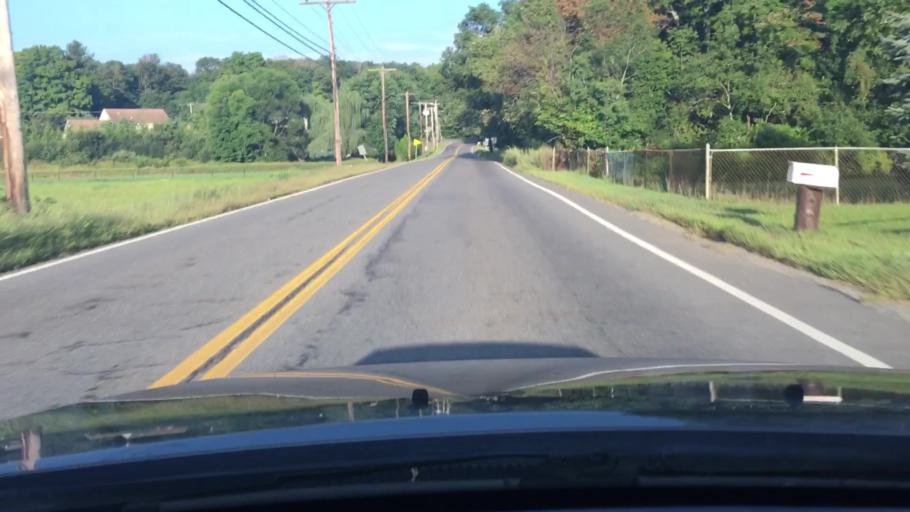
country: US
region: Massachusetts
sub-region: Worcester County
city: Westborough
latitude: 42.2579
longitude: -71.6034
